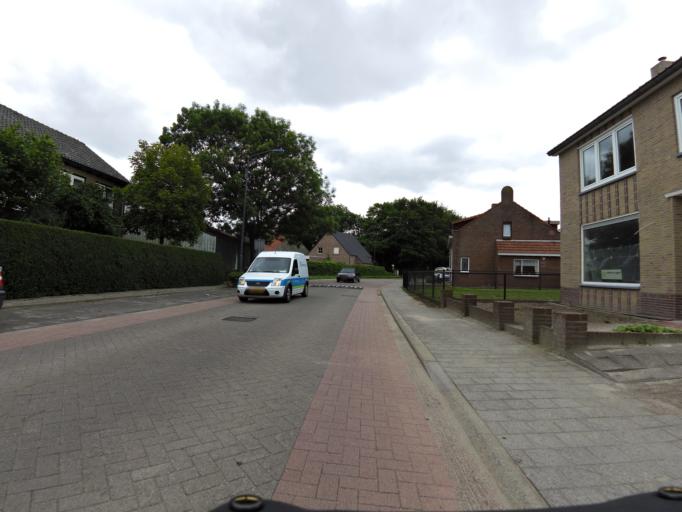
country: NL
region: North Brabant
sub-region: Gemeente Baarle-Nassau
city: Baarle-Nassau
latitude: 51.4435
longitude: 4.9209
